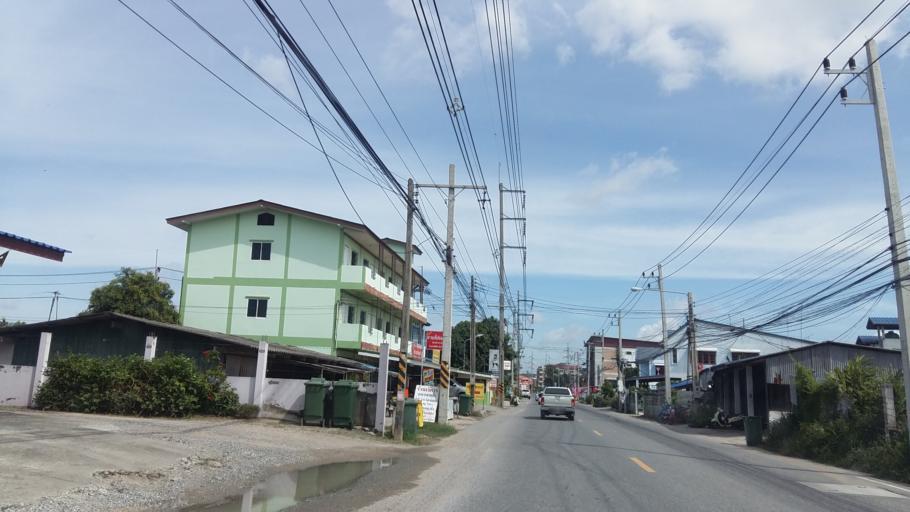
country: TH
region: Chon Buri
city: Phan Thong
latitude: 13.4355
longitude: 101.0613
